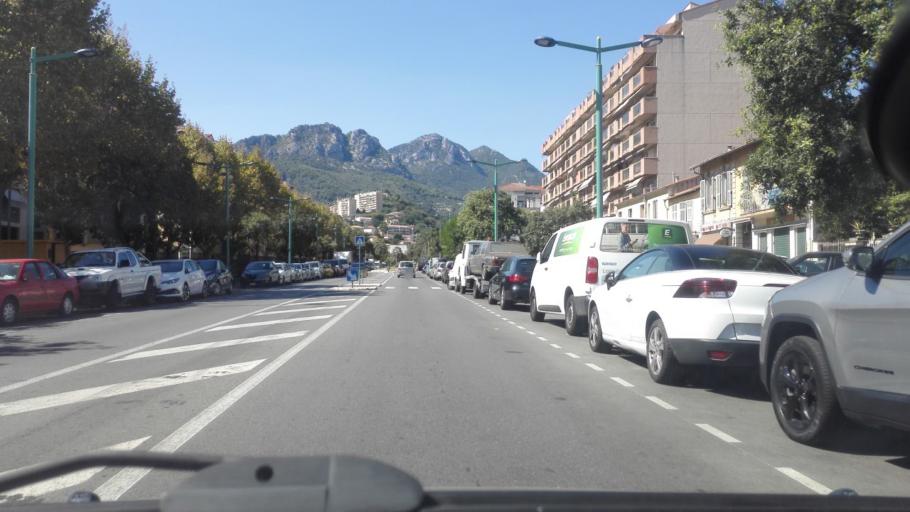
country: FR
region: Provence-Alpes-Cote d'Azur
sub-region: Departement des Alpes-Maritimes
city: Roquebrune-Cap-Martin
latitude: 43.7746
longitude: 7.4894
